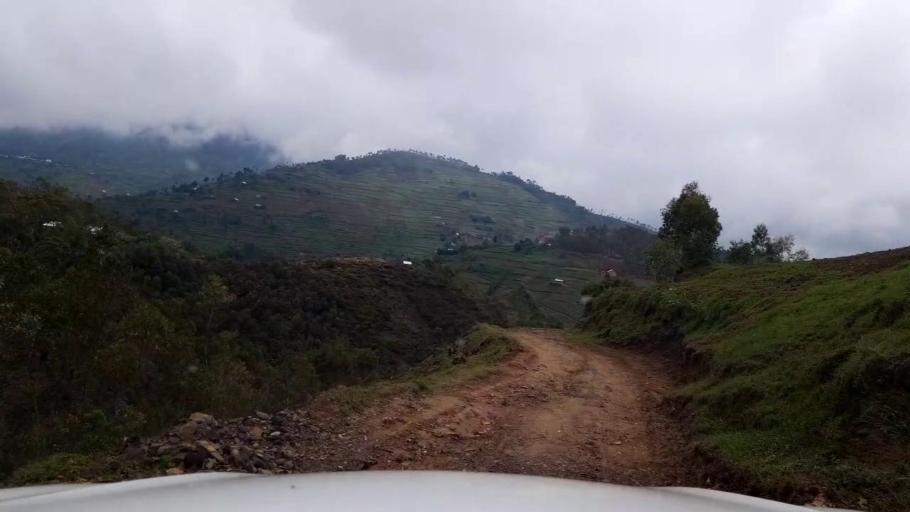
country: RW
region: Northern Province
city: Musanze
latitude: -1.5953
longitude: 29.7754
